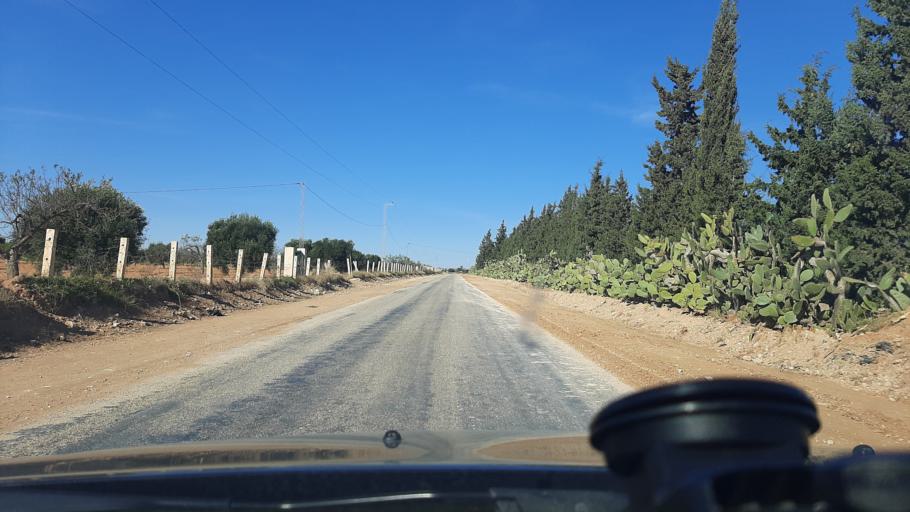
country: TN
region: Safaqis
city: Sfax
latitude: 34.9141
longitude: 10.5869
